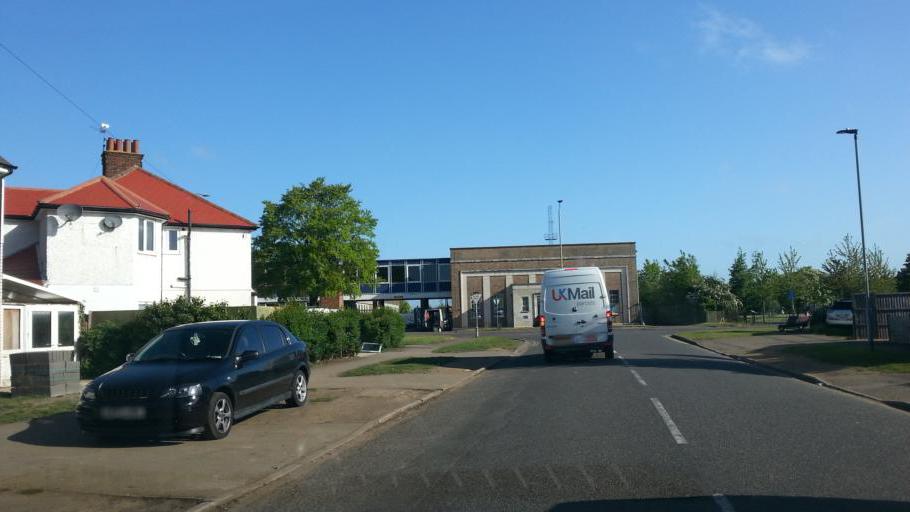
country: GB
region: England
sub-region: Peterborough
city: Peterborough
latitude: 52.5825
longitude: -0.2610
